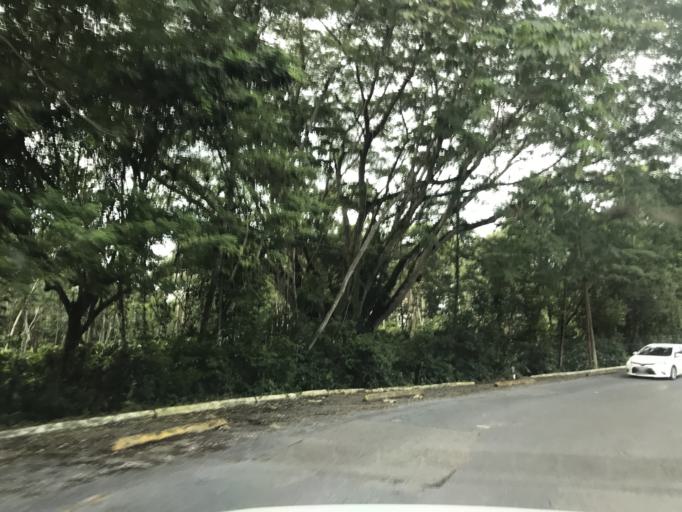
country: GT
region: Izabal
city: Morales
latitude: 15.6415
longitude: -89.0101
